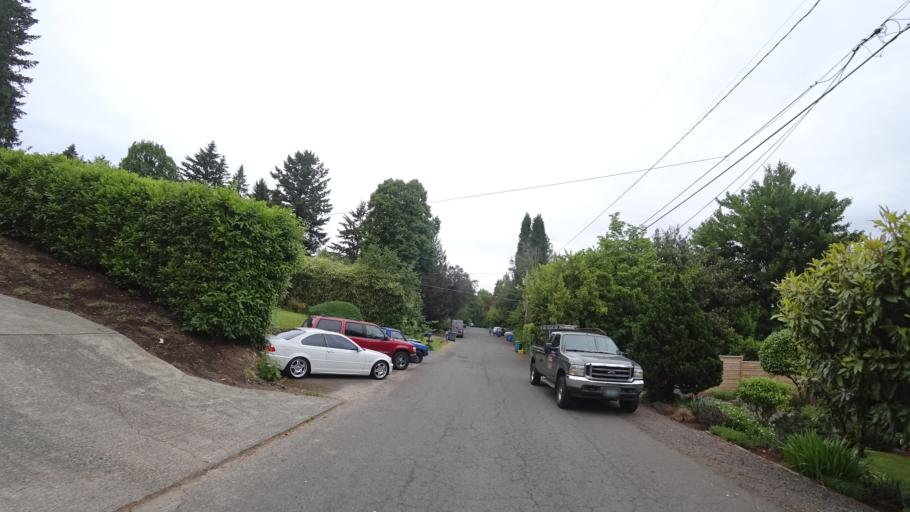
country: US
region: Oregon
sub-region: Clackamas County
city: Lake Oswego
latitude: 45.4571
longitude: -122.6779
